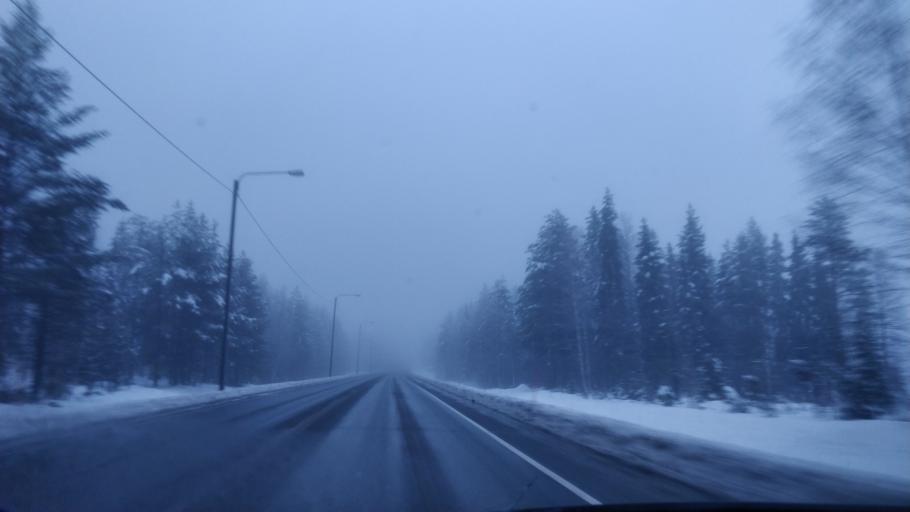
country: FI
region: Lapland
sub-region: Kemi-Tornio
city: Tervola
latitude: 66.1321
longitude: 24.9031
